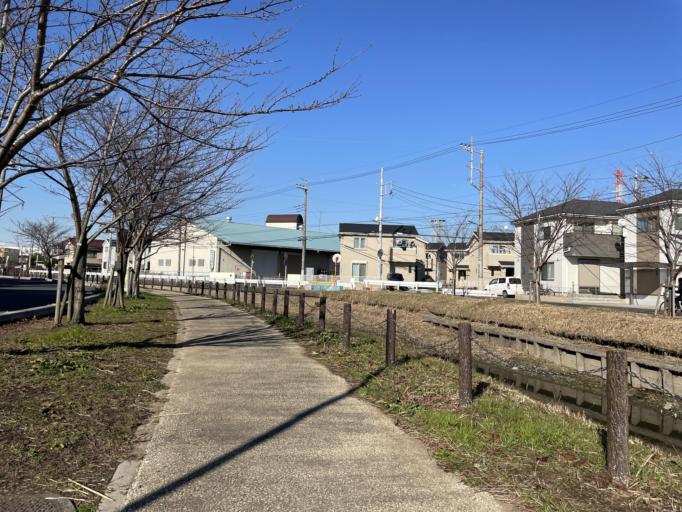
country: JP
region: Saitama
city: Yashio-shi
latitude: 35.8458
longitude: 139.8260
